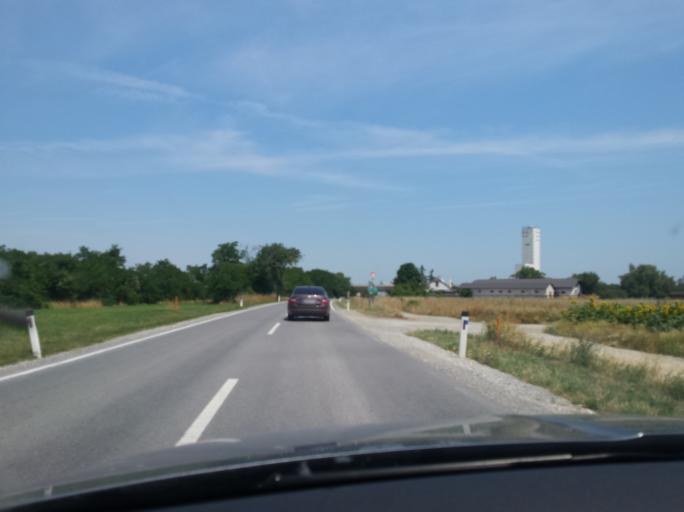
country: AT
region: Lower Austria
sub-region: Politischer Bezirk Bruck an der Leitha
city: Petronell-Carnuntum
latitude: 48.1013
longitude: 16.8637
